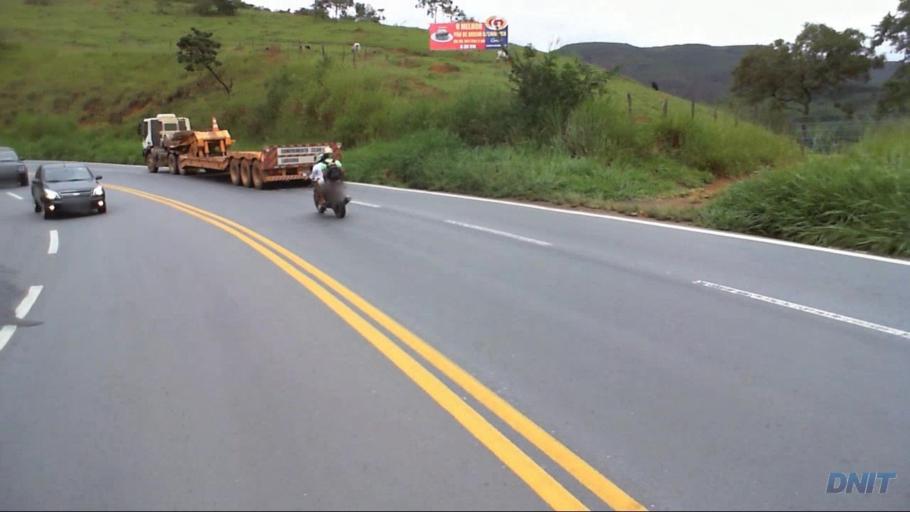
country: BR
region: Minas Gerais
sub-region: Barao De Cocais
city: Barao de Cocais
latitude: -19.8352
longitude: -43.3733
